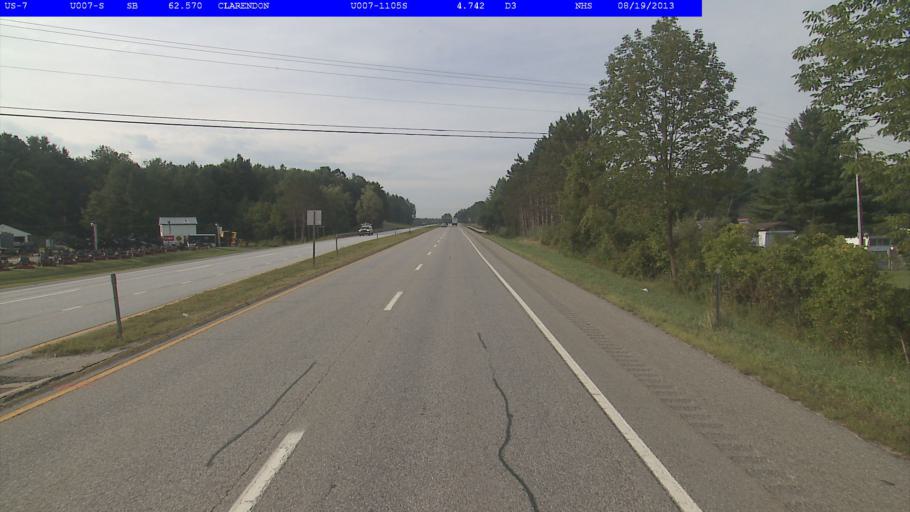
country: US
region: Vermont
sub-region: Rutland County
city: Rutland
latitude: 43.5599
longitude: -72.9645
